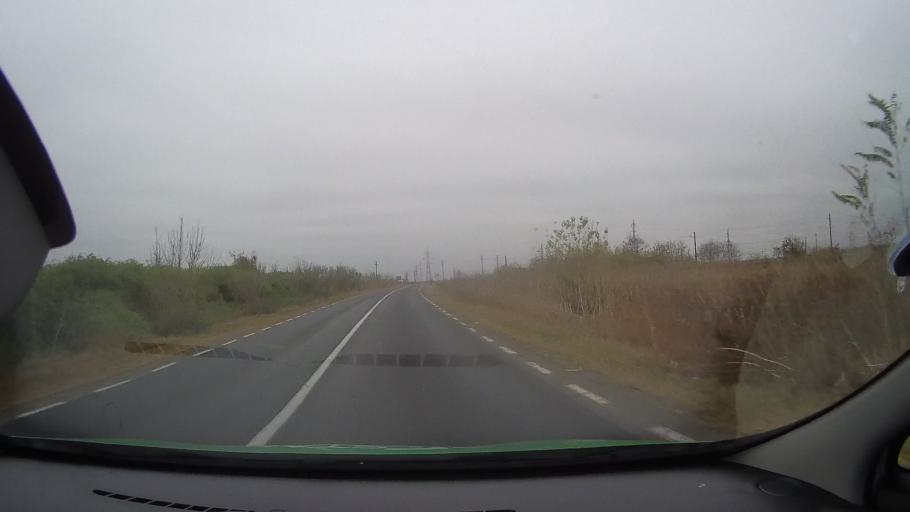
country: RO
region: Braila
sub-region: Comuna Baraganul
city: Baraganul
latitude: 44.7971
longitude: 27.5124
